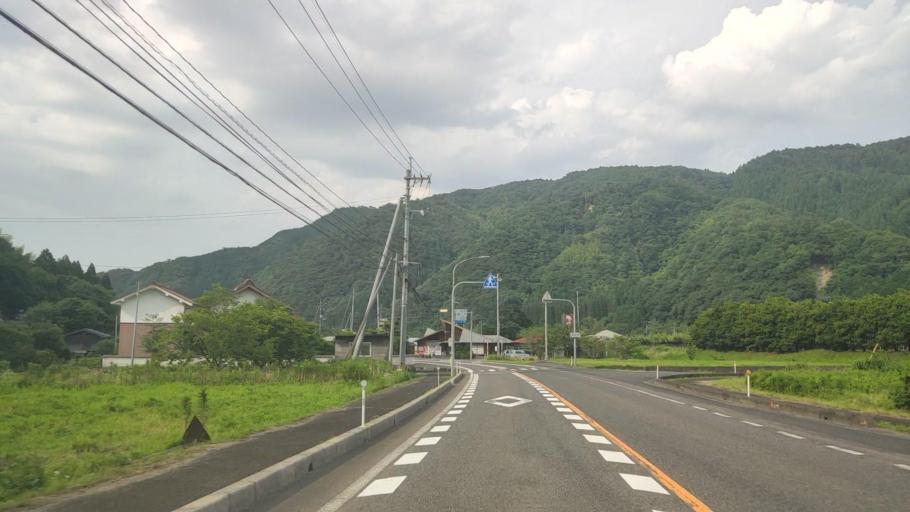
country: JP
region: Tottori
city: Kurayoshi
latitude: 35.3653
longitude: 133.8492
